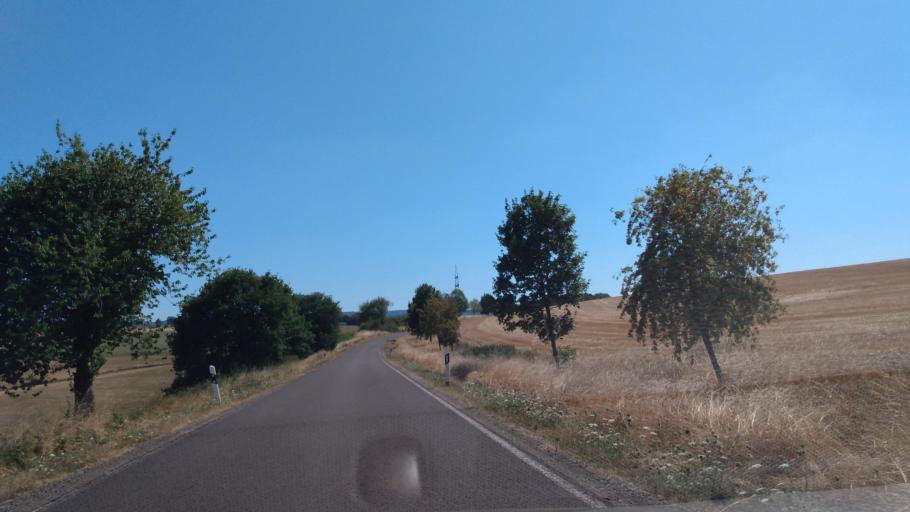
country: DE
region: Rheinland-Pfalz
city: Rorodt
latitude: 49.7915
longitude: 7.0513
